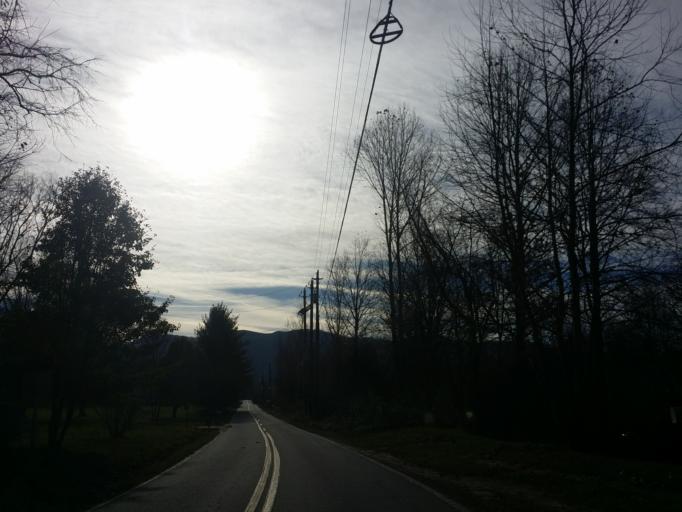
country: US
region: North Carolina
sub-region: Buncombe County
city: Swannanoa
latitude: 35.6212
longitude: -82.4312
